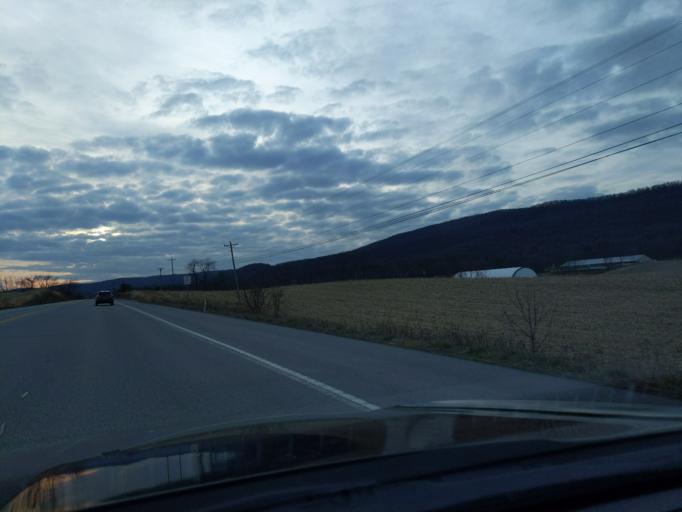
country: US
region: Pennsylvania
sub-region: Blair County
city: Williamsburg
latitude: 40.5371
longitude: -78.1879
